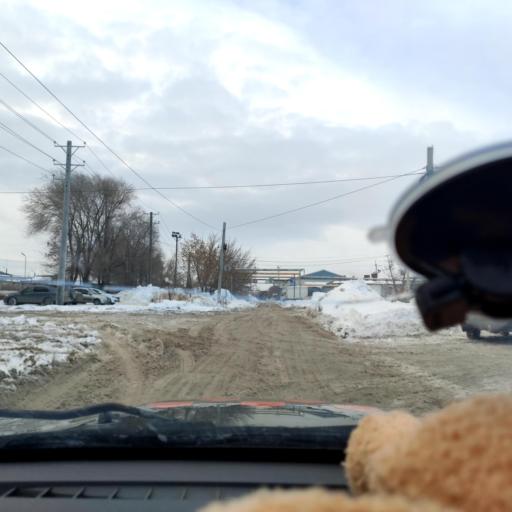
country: RU
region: Samara
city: Tol'yatti
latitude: 53.5766
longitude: 49.2840
